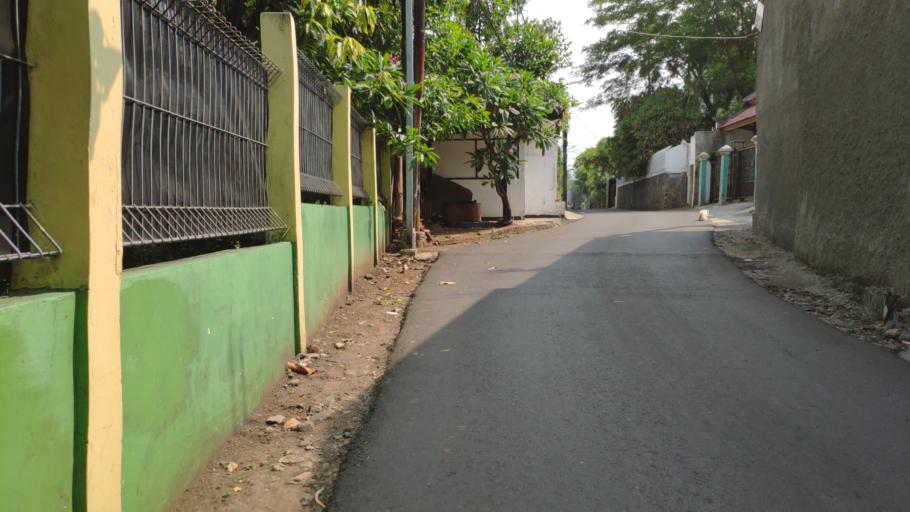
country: ID
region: Jakarta Raya
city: Jakarta
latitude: -6.2723
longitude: 106.8198
